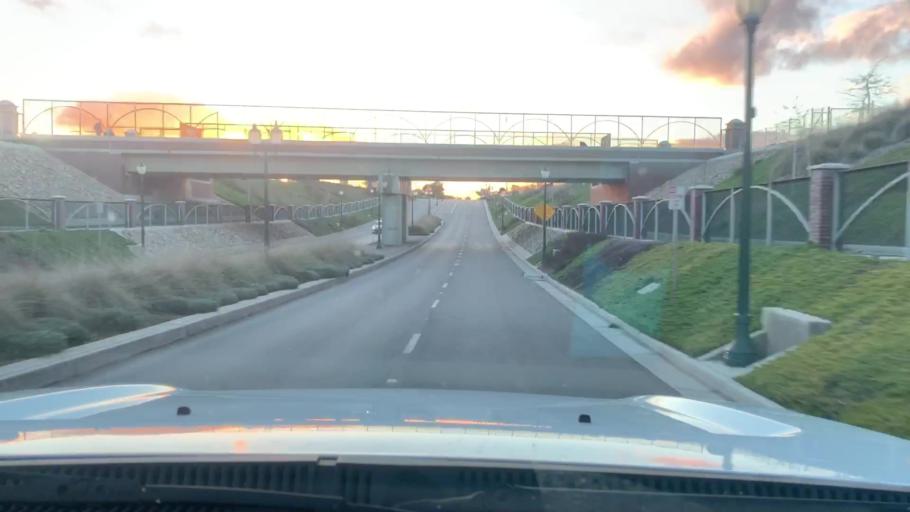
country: US
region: California
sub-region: Tulare County
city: Tulare
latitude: 36.1966
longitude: -119.3453
